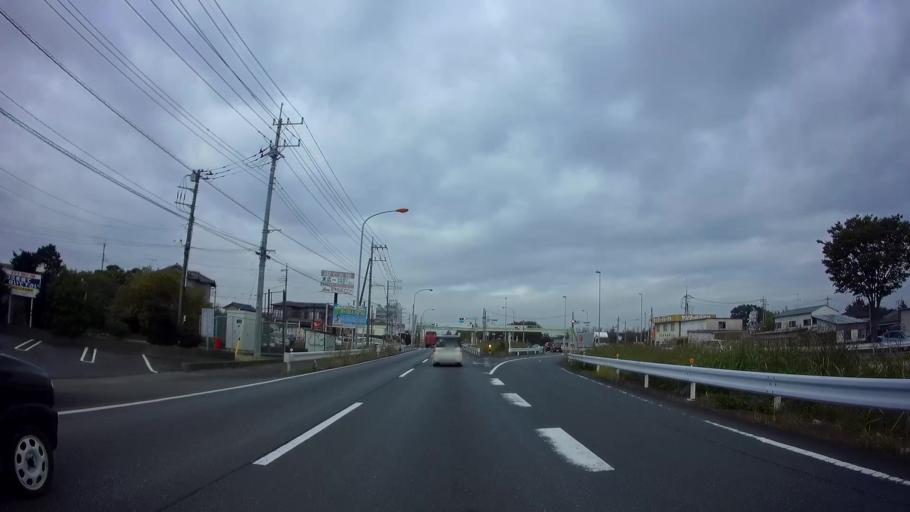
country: JP
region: Saitama
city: Kumagaya
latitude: 36.1567
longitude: 139.4098
